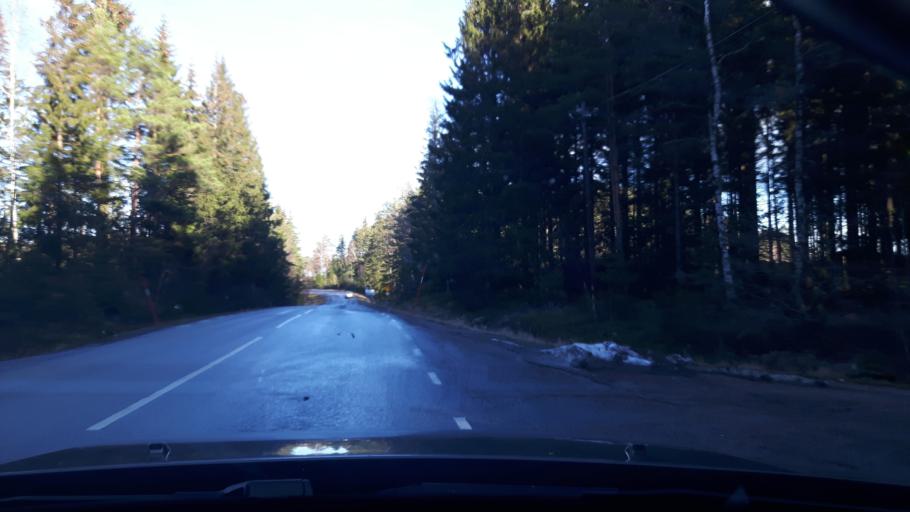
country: SE
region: Vaestra Goetaland
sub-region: Munkedals Kommun
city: Munkedal
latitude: 58.5142
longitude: 11.6832
